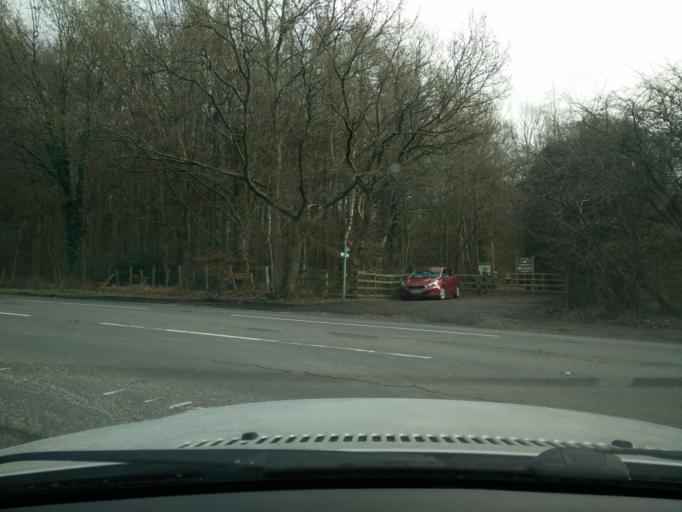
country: GB
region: England
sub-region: Buckinghamshire
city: Great Missenden
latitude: 51.6613
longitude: -0.6785
